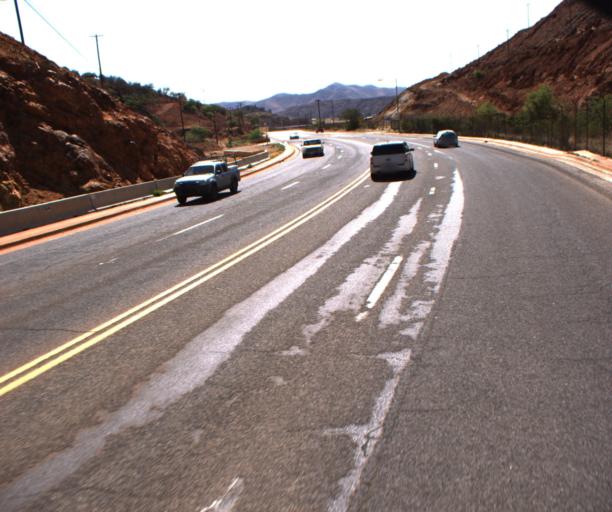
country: US
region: Arizona
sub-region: Cochise County
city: Bisbee
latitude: 31.4378
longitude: -109.9069
